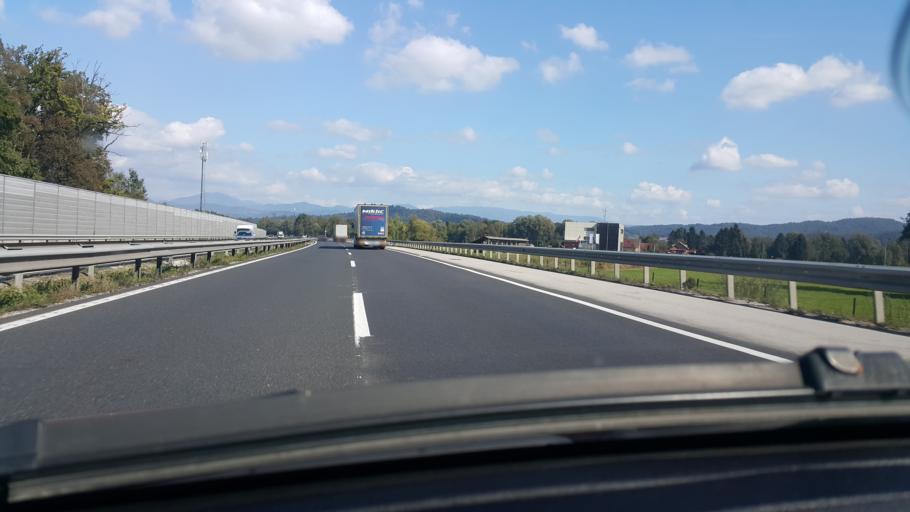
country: SI
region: Dol pri Ljubljani
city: Dol pri Ljubljani
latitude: 46.1033
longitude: 14.5959
